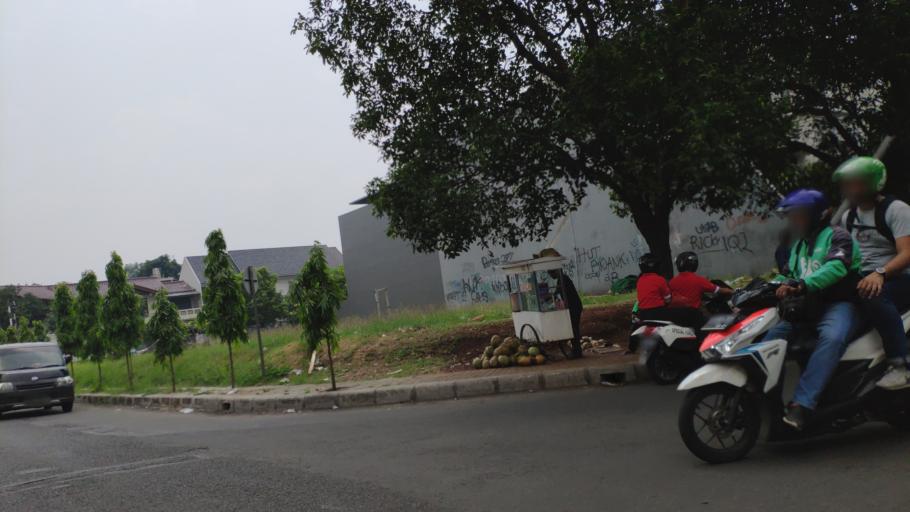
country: ID
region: Banten
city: South Tangerang
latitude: -6.2656
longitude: 106.7796
